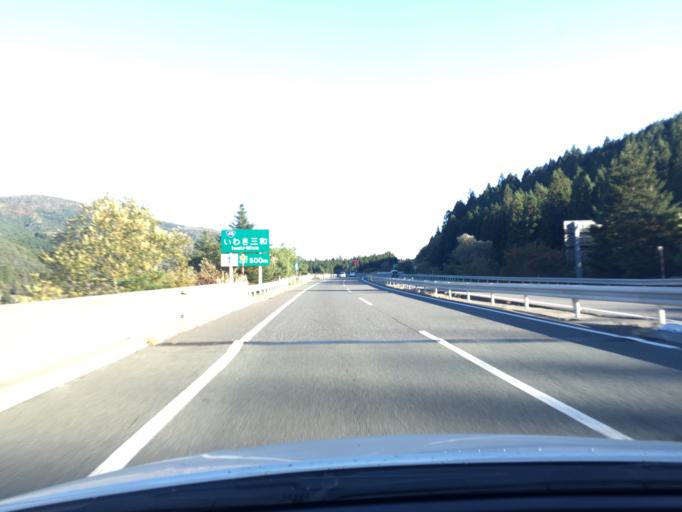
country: JP
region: Fukushima
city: Iwaki
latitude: 37.1071
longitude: 140.7637
